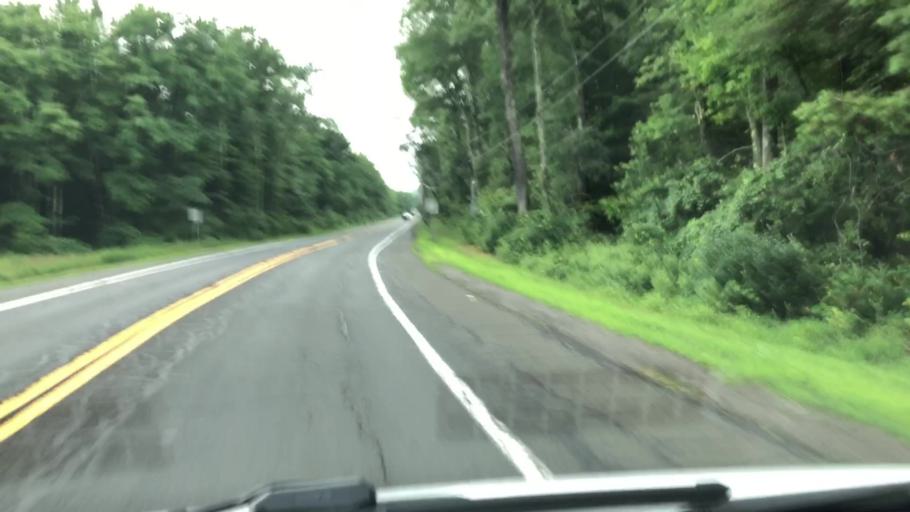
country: US
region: Massachusetts
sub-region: Franklin County
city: South Deerfield
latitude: 42.4621
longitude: -72.6192
